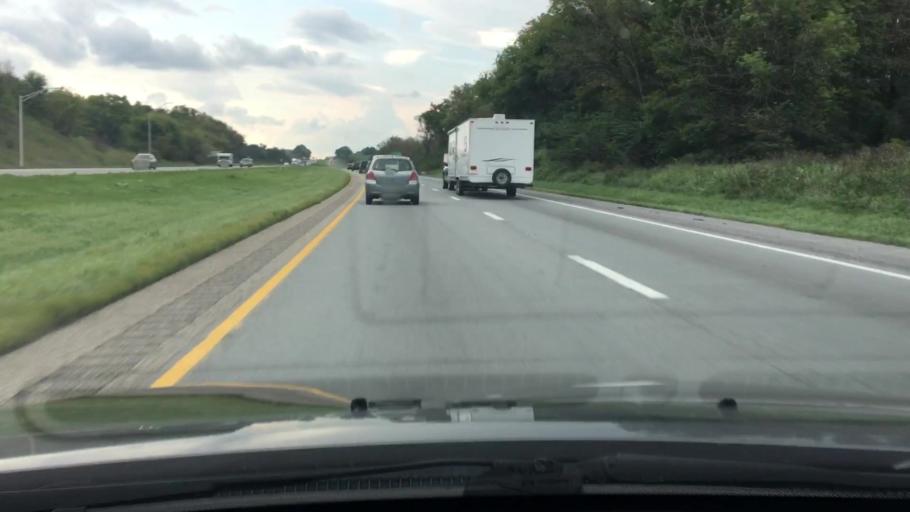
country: US
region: Pennsylvania
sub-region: Cumberland County
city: Newville
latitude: 40.1320
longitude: -77.3449
